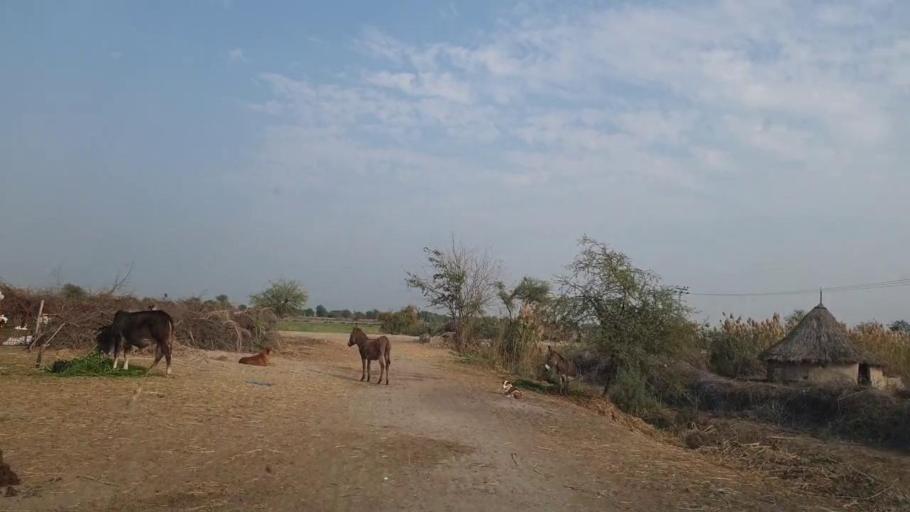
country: PK
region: Sindh
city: Pithoro
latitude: 25.5628
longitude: 69.2076
